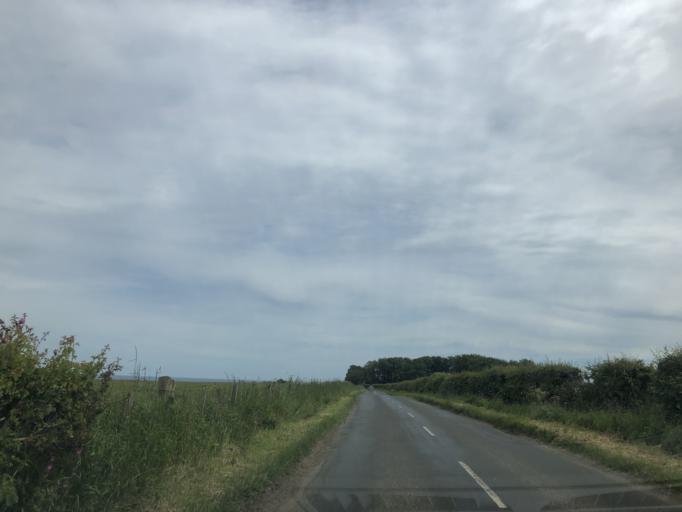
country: GB
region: Scotland
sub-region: Fife
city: Anstruther
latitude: 56.2668
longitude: -2.6538
